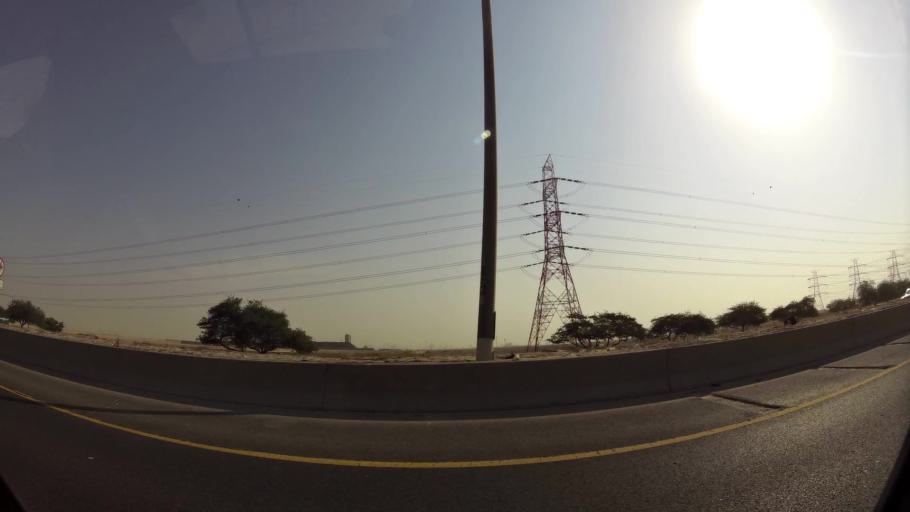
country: KW
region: Al Ahmadi
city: Al Ahmadi
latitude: 29.0145
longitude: 48.0927
